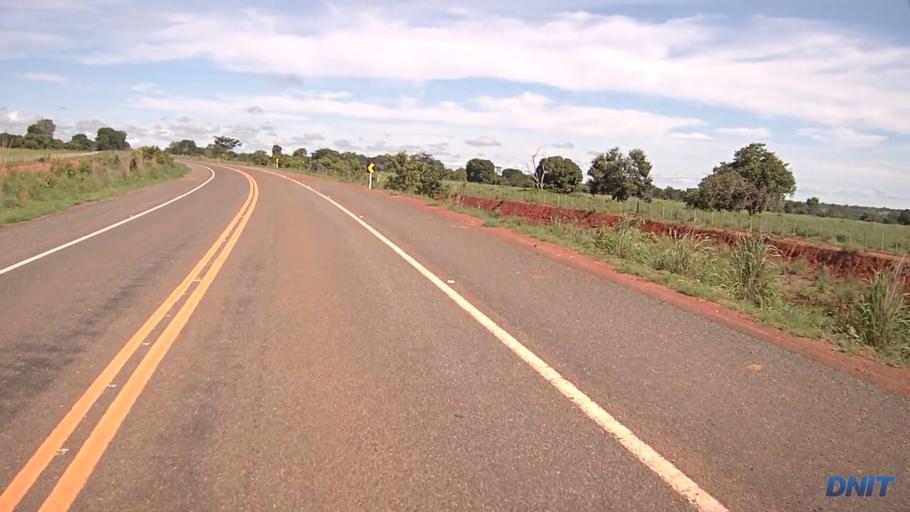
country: BR
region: Goias
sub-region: Sao Miguel Do Araguaia
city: Sao Miguel do Araguaia
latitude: -13.3201
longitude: -50.1598
